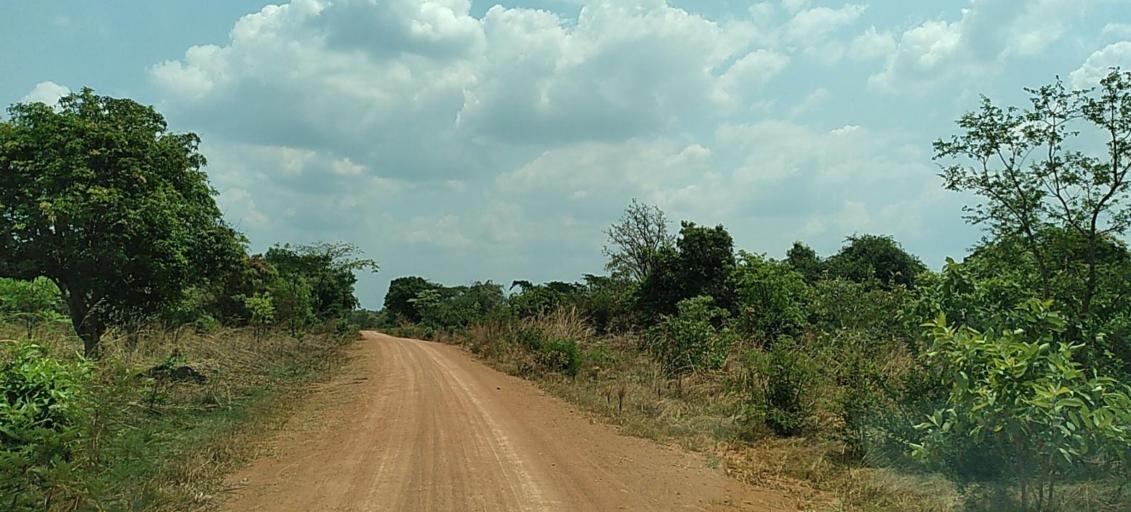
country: ZM
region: Copperbelt
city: Luanshya
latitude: -13.1459
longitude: 28.3166
